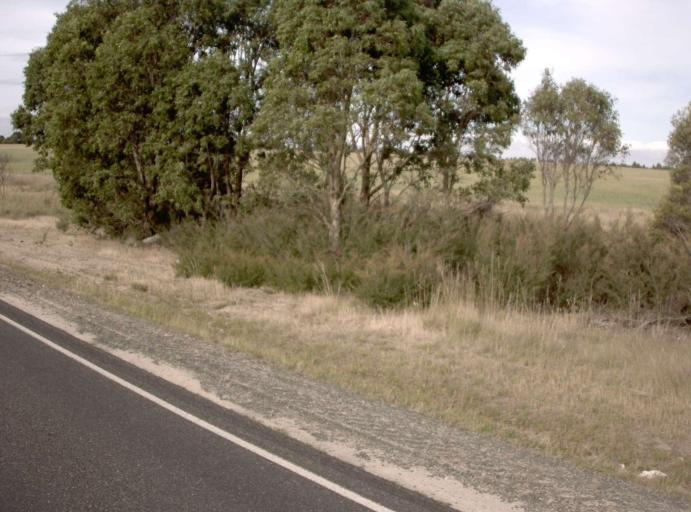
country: AU
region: Victoria
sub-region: Wellington
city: Heyfield
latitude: -38.0447
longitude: 146.6650
